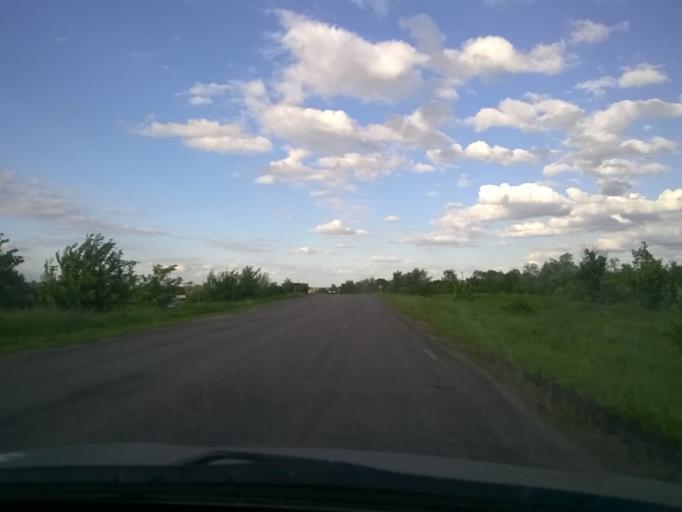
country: RU
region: Volgograd
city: Uryupinsk
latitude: 50.8348
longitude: 42.0907
